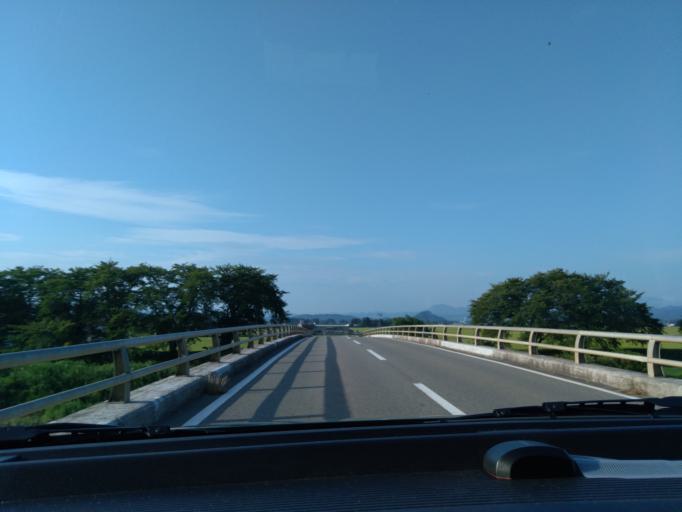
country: JP
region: Akita
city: Kakunodatemachi
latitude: 39.5408
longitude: 140.5577
